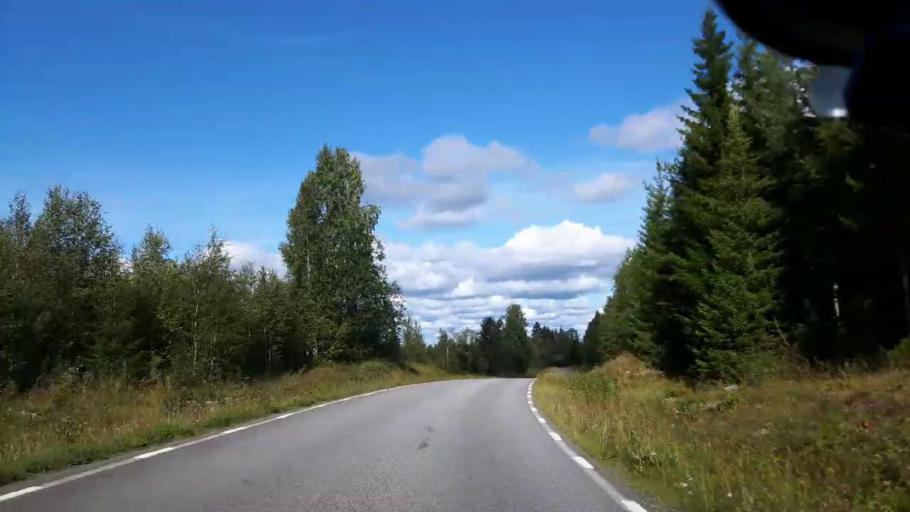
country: SE
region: Jaemtland
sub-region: OEstersunds Kommun
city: Brunflo
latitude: 63.2160
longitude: 15.2447
